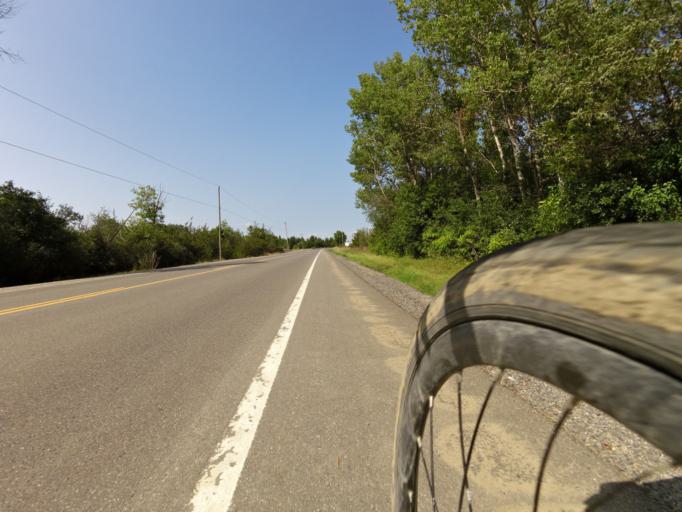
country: CA
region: Ontario
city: Skatepark
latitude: 44.2616
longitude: -76.7239
